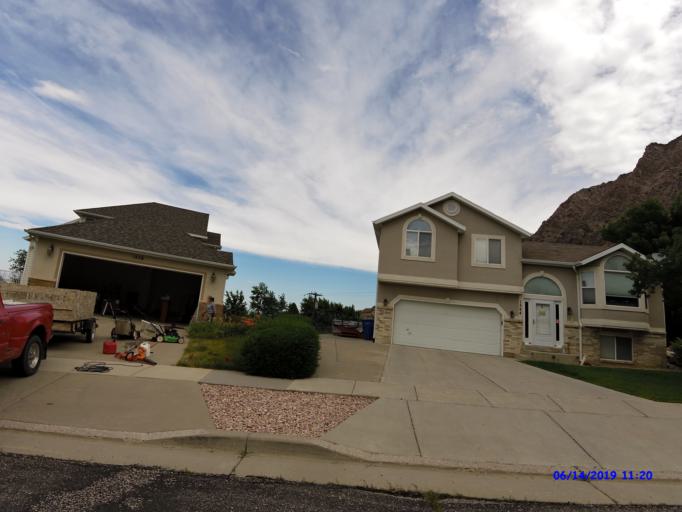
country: US
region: Utah
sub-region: Weber County
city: Ogden
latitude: 41.2560
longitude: -111.9388
